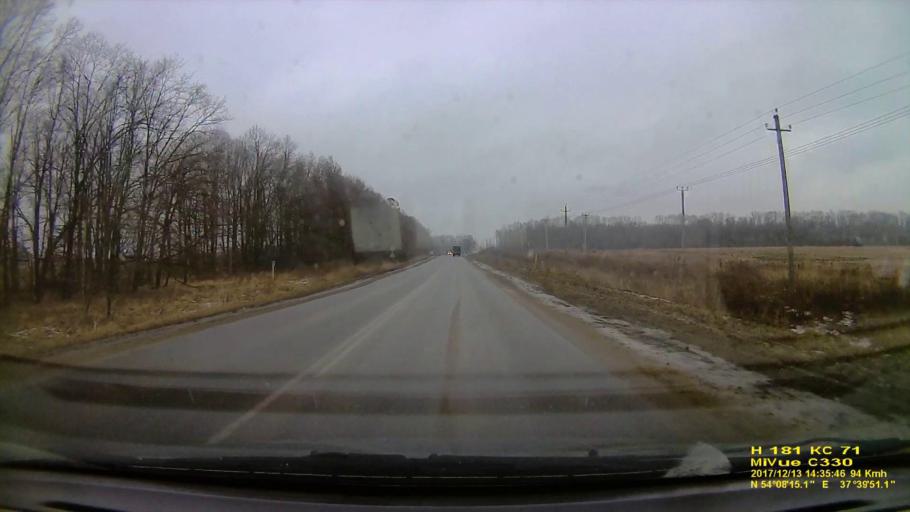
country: RU
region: Tula
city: Skuratovskiy
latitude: 54.1376
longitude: 37.6642
